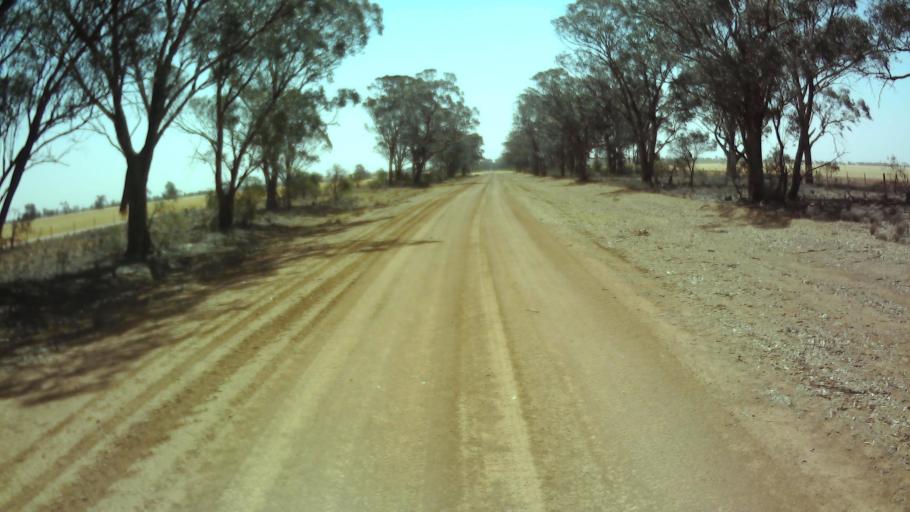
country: AU
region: New South Wales
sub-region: Weddin
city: Grenfell
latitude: -33.9205
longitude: 147.7791
